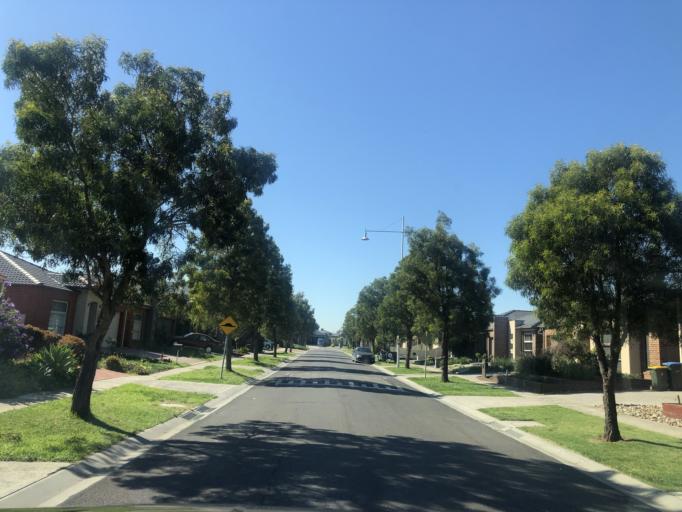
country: AU
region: Victoria
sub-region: Wyndham
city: Point Cook
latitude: -37.9112
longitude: 144.7254
